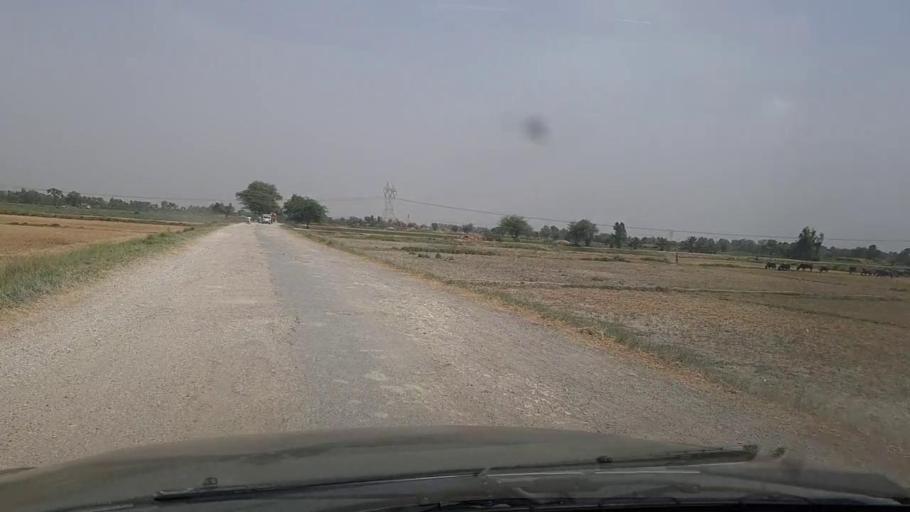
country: PK
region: Sindh
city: Shikarpur
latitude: 27.9222
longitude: 68.6742
